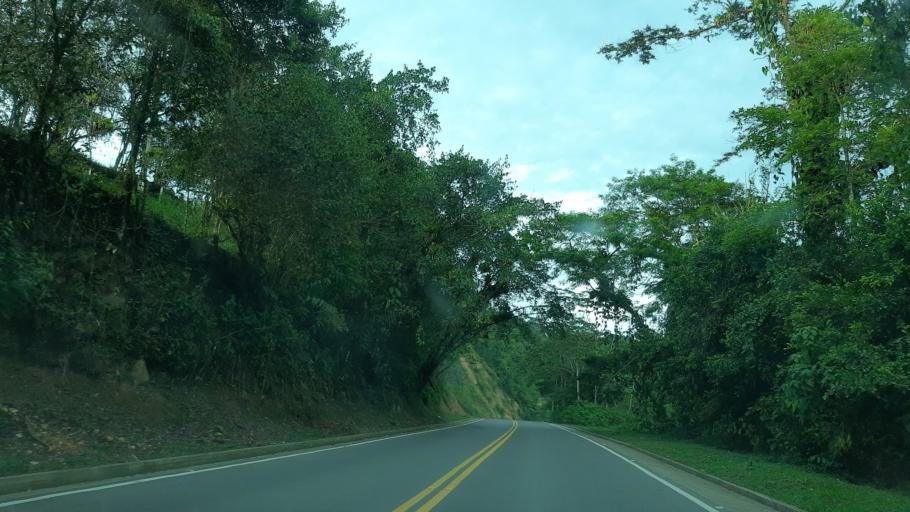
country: CO
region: Boyaca
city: San Luis de Gaceno
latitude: 4.8316
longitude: -73.1307
